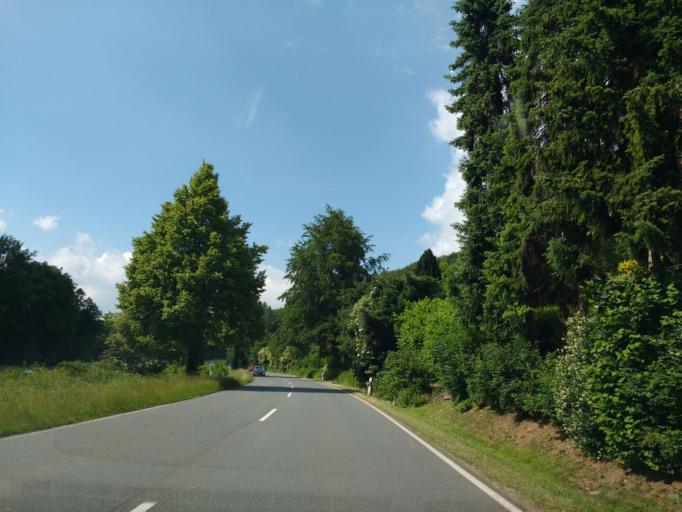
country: DE
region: North Rhine-Westphalia
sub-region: Regierungsbezirk Detmold
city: Dorentrup
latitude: 52.1144
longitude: 8.9529
